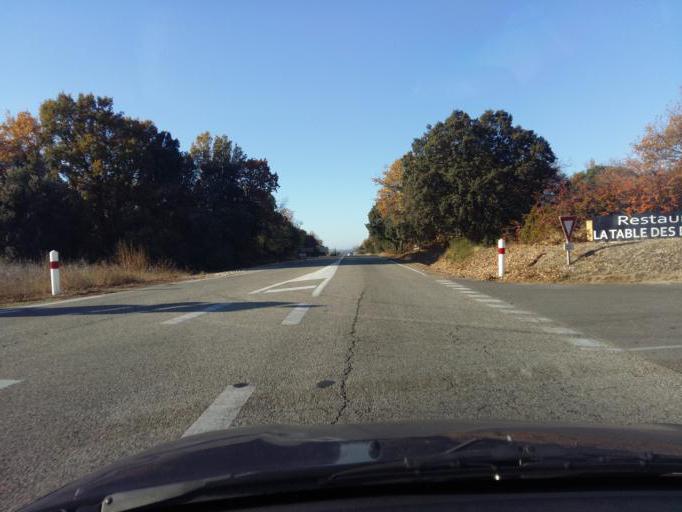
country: FR
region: Rhone-Alpes
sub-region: Departement de la Drome
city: Grignan
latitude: 44.4192
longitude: 4.8972
